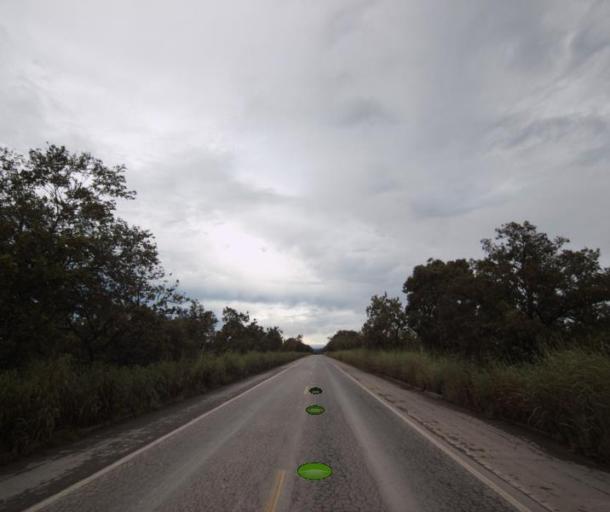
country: BR
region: Goias
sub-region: Porangatu
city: Porangatu
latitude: -13.5407
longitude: -49.1055
